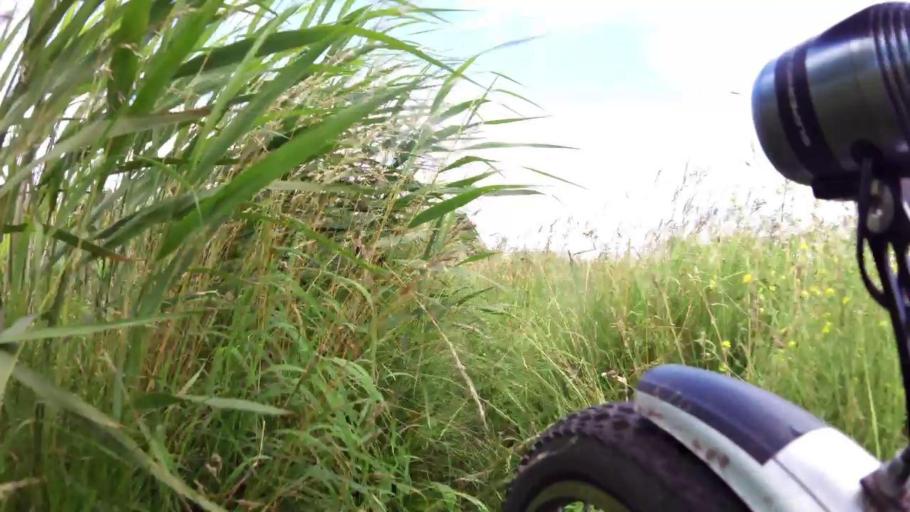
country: PL
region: West Pomeranian Voivodeship
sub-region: Powiat bialogardzki
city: Bialogard
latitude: 53.9975
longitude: 15.9829
